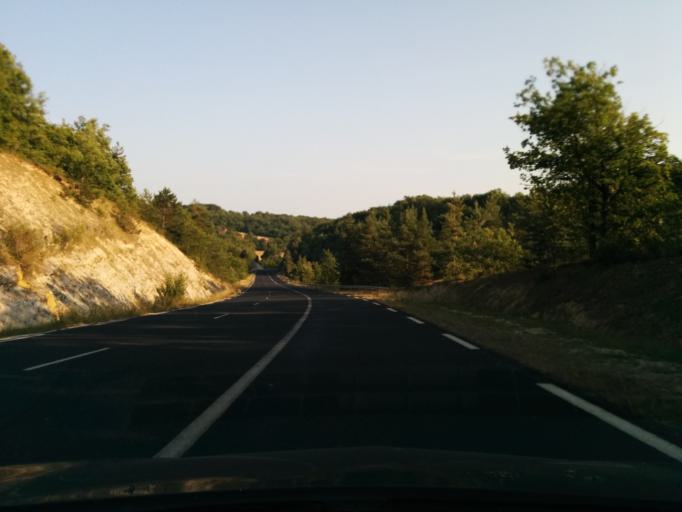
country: FR
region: Midi-Pyrenees
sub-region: Departement du Lot
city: Le Vigan
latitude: 44.7152
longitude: 1.4820
